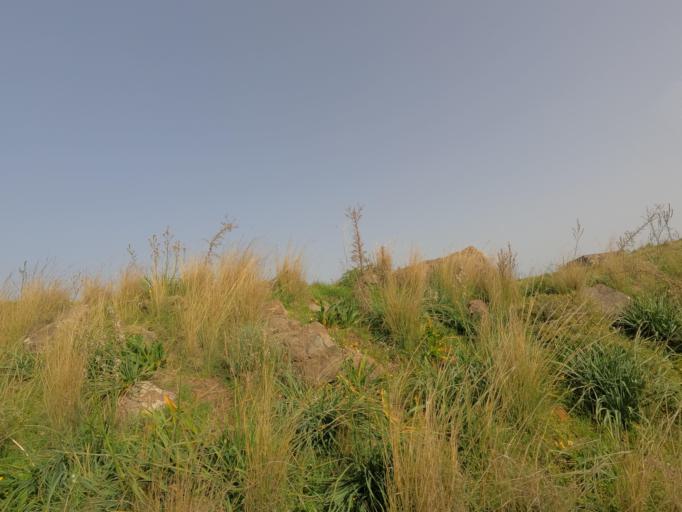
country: CY
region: Pafos
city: Polis
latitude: 34.9984
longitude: 32.3620
